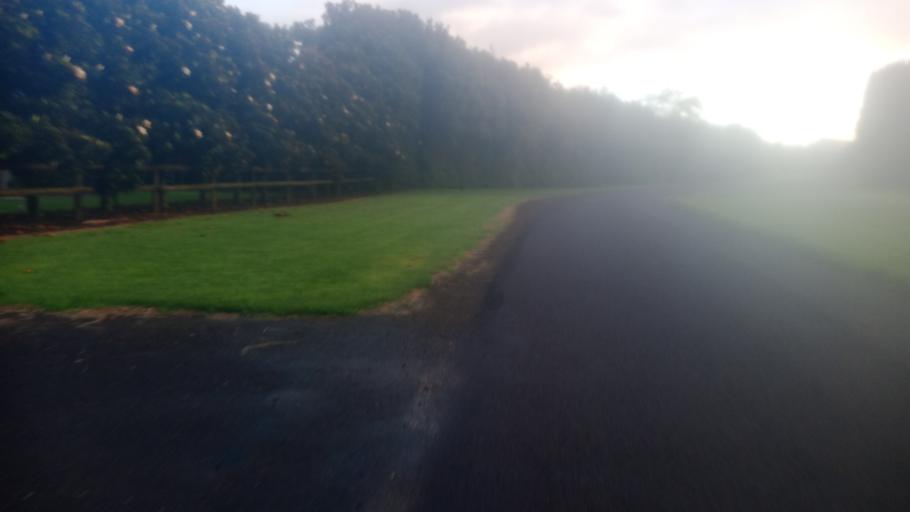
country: NZ
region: Gisborne
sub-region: Gisborne District
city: Gisborne
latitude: -38.6419
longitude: 177.9883
